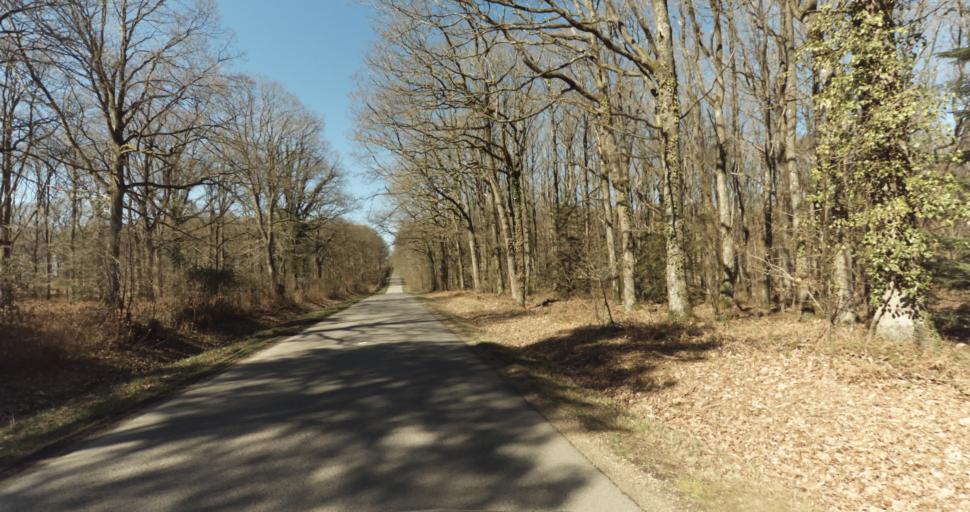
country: FR
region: Lower Normandy
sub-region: Departement du Calvados
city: Livarot
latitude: 48.9663
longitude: 0.0866
